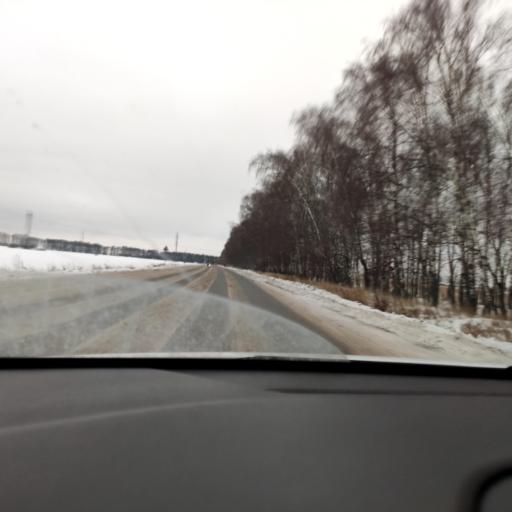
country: RU
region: Tatarstan
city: Osinovo
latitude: 55.8935
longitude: 48.8898
